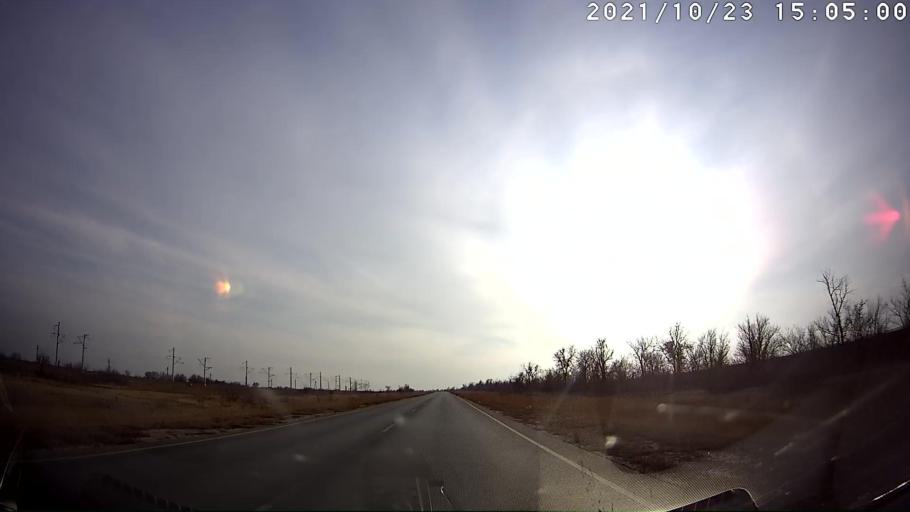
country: RU
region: Volgograd
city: Volgograd
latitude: 48.3912
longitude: 44.3631
